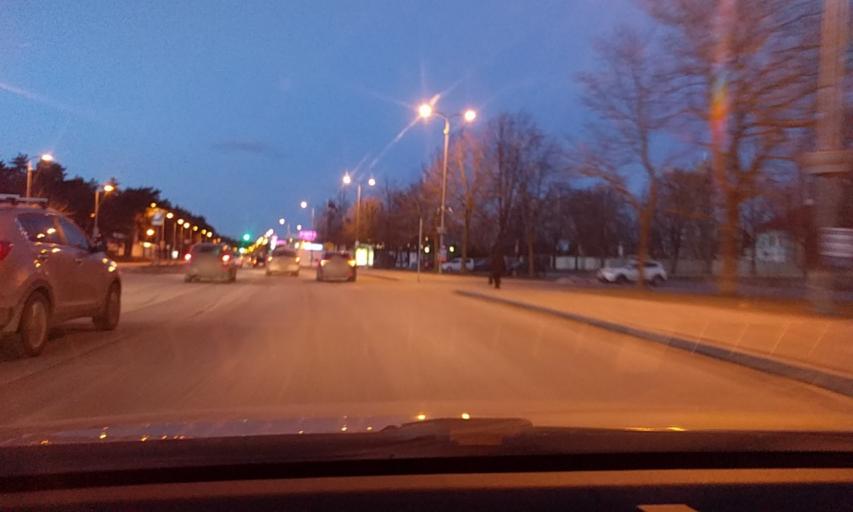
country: EE
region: Harju
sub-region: Viimsi vald
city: Viimsi
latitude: 59.4666
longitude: 24.8334
